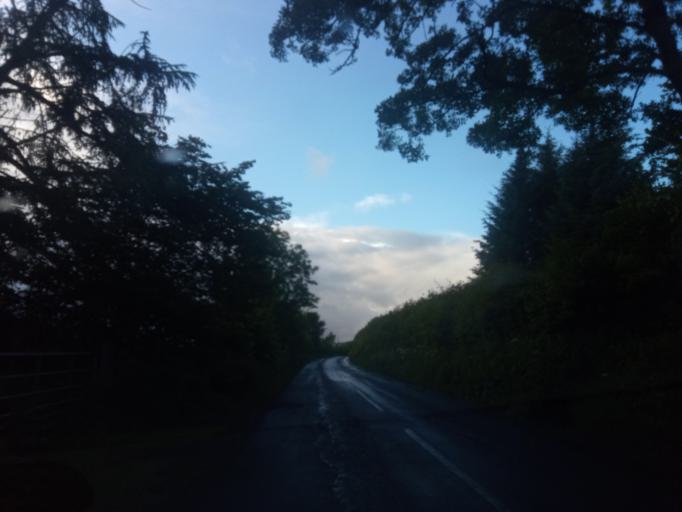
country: GB
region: England
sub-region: Northumberland
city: Bardon Mill
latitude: 54.8730
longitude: -2.2531
